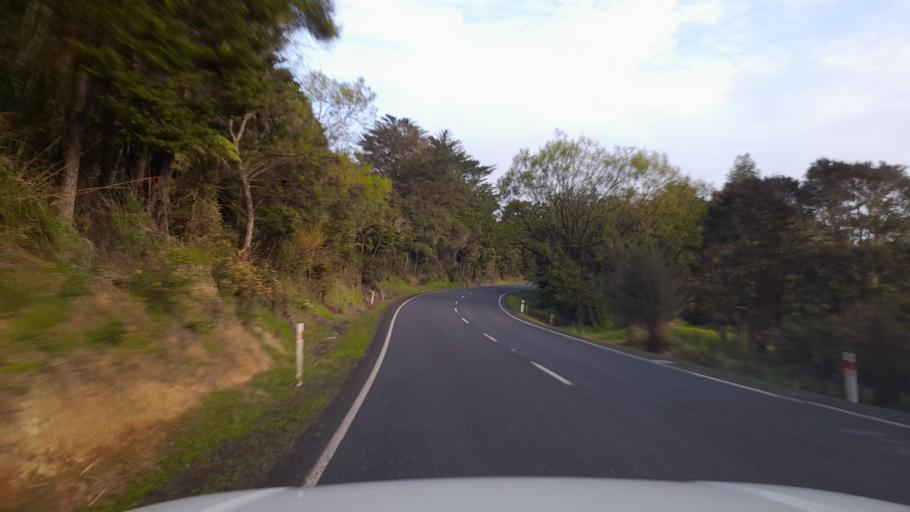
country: NZ
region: Northland
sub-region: Kaipara District
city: Dargaville
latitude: -35.6541
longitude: 173.8737
